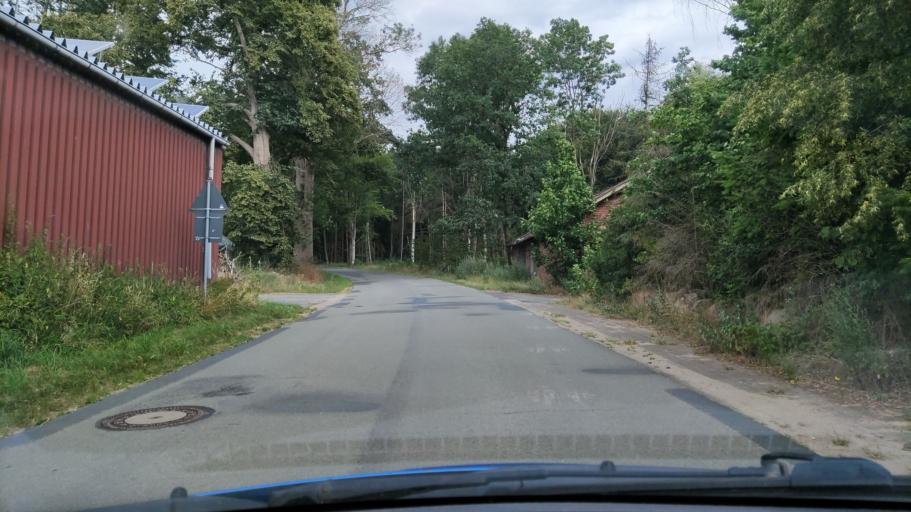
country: DE
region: Lower Saxony
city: Suhlendorf
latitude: 52.9531
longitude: 10.8262
